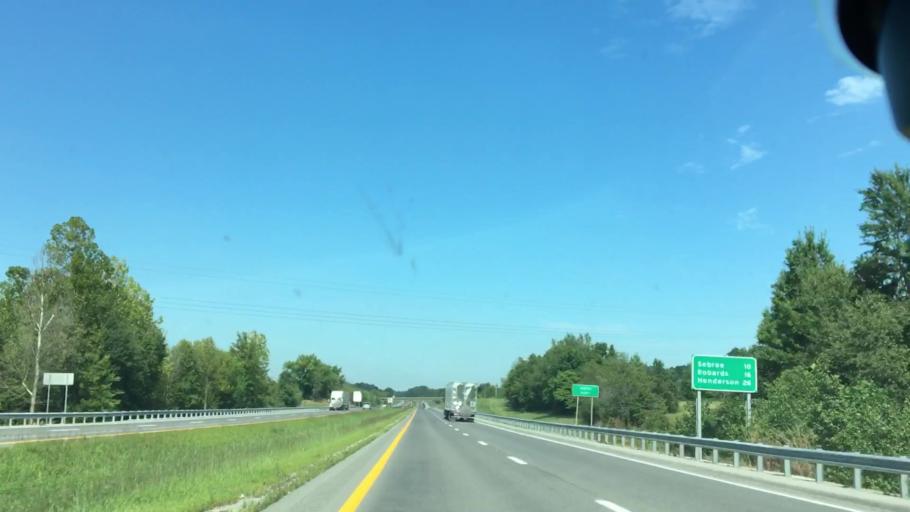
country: US
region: Kentucky
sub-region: Webster County
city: Sebree
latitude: 37.5029
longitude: -87.4751
